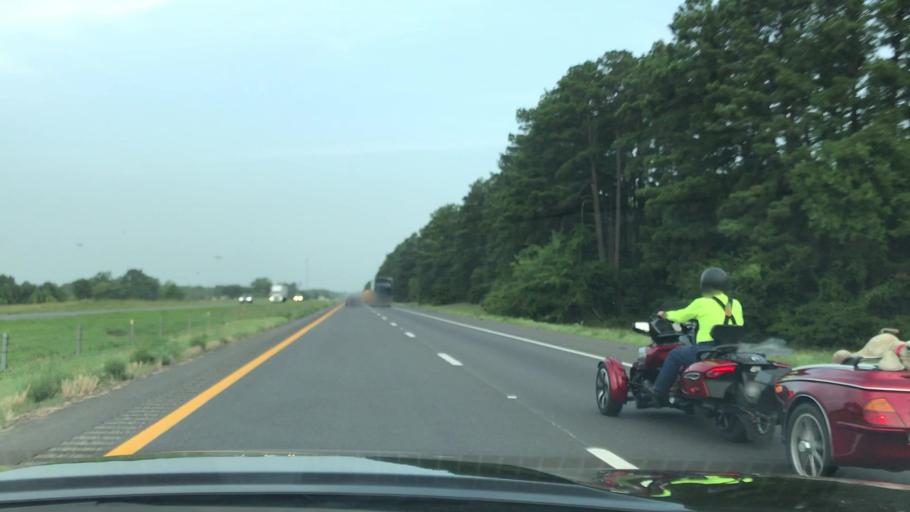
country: US
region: Texas
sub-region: Harrison County
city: Hallsville
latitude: 32.4663
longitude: -94.6254
